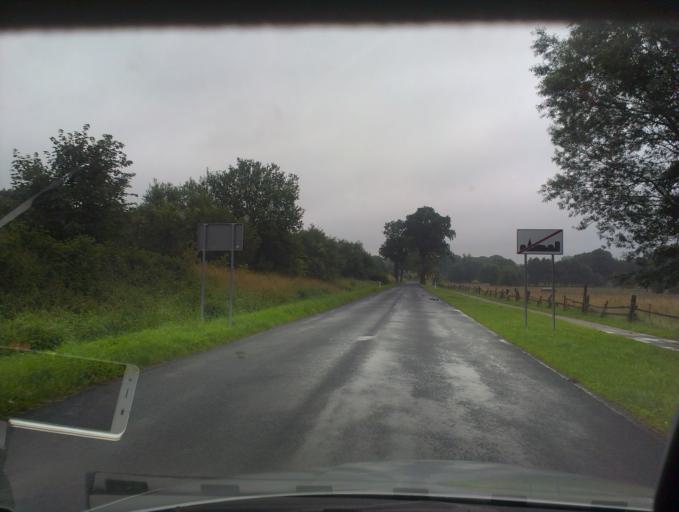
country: PL
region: West Pomeranian Voivodeship
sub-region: Powiat szczecinecki
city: Barwice
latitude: 53.7531
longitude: 16.3623
